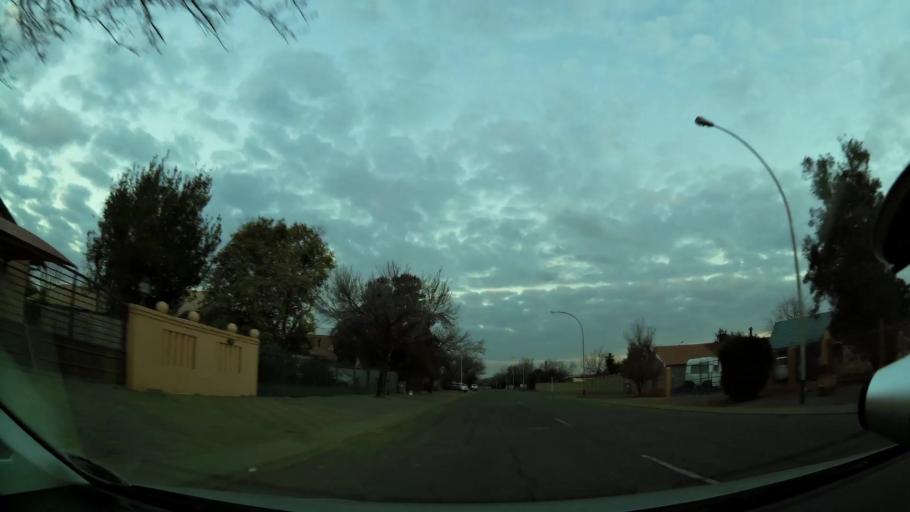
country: ZA
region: Orange Free State
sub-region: Mangaung Metropolitan Municipality
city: Bloemfontein
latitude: -29.1689
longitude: 26.1856
